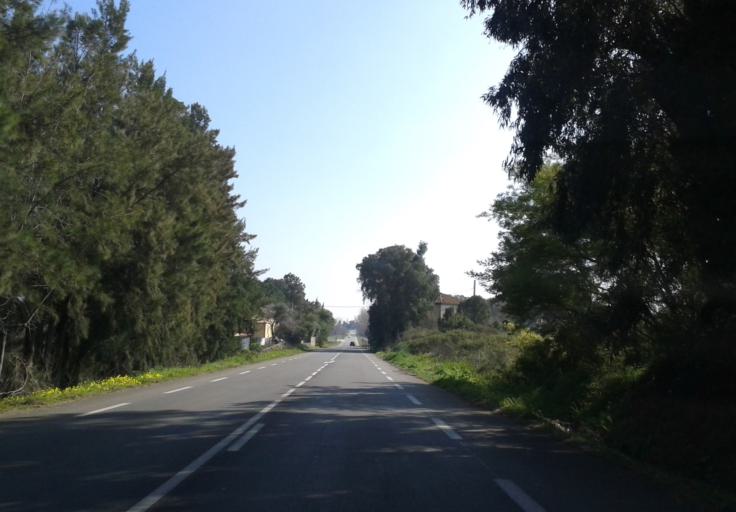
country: FR
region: Corsica
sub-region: Departement de la Haute-Corse
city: Cervione
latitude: 42.2955
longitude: 9.5462
